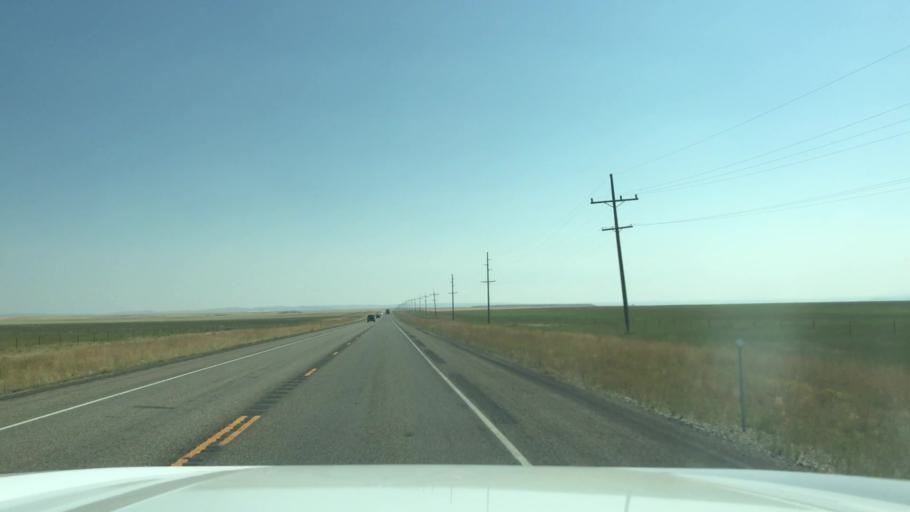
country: US
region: Montana
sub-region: Wheatland County
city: Harlowton
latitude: 46.5178
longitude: -109.7661
